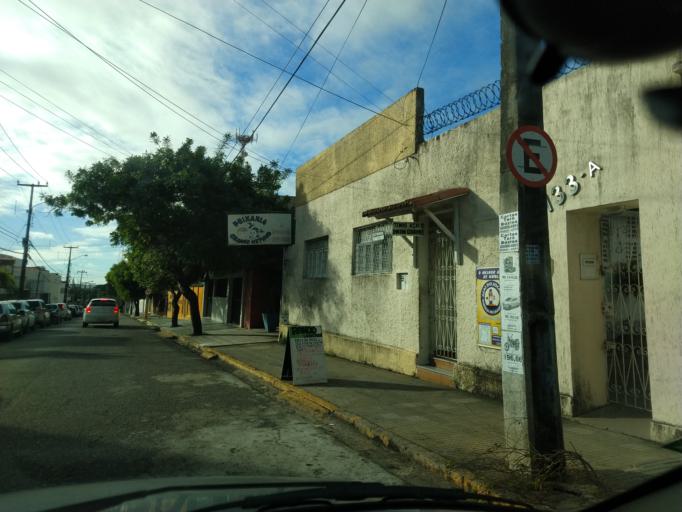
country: BR
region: Rio Grande do Norte
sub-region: Natal
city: Natal
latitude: -5.7935
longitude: -35.2093
